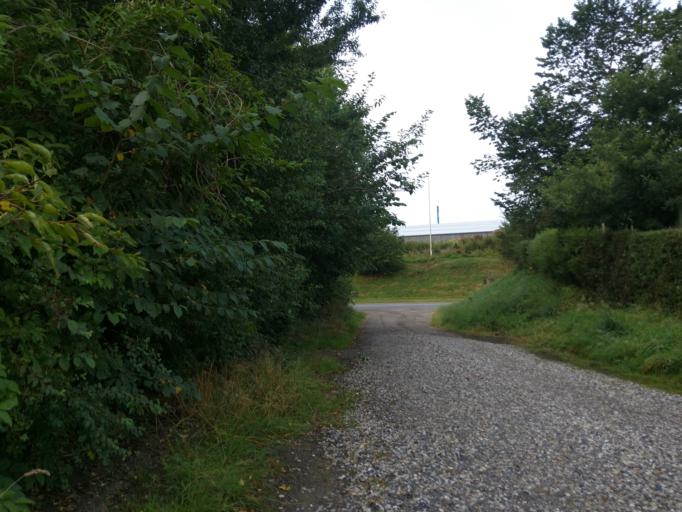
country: DK
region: Central Jutland
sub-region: Viborg Kommune
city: Viborg
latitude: 56.4531
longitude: 9.3785
